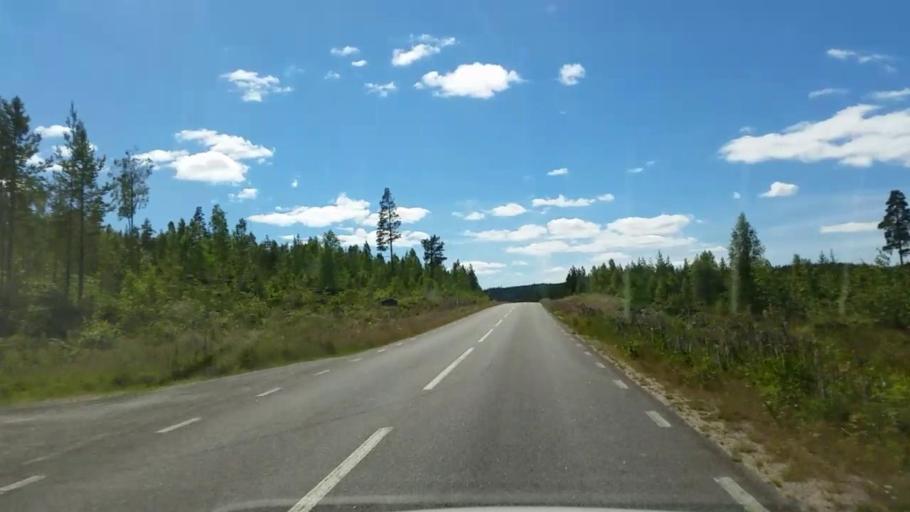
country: SE
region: Gaevleborg
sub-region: Ljusdals Kommun
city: Farila
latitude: 61.6213
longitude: 15.5502
